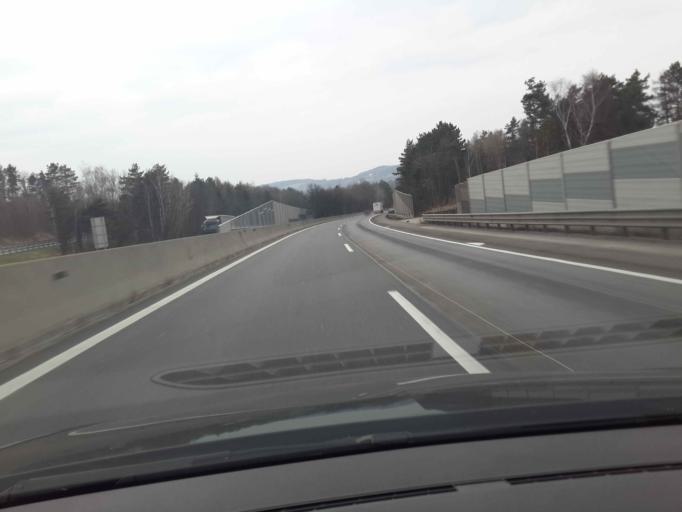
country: AT
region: Lower Austria
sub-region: Politischer Bezirk Sankt Polten
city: Eichgraben
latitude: 48.1518
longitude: 15.9719
